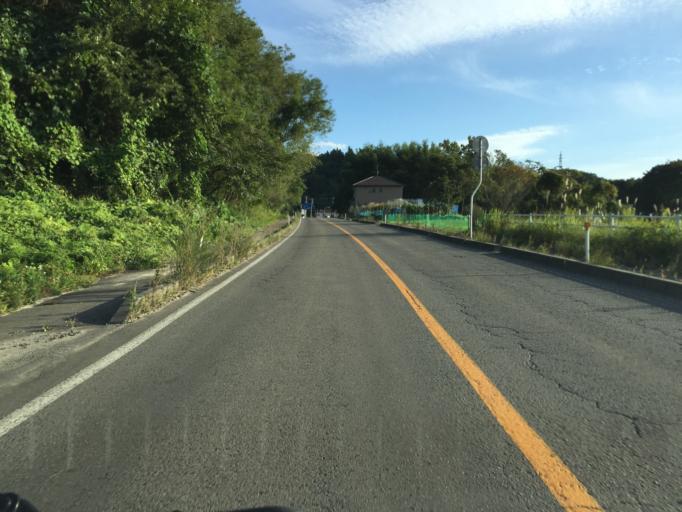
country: JP
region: Fukushima
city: Hobaramachi
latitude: 37.6690
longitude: 140.6130
